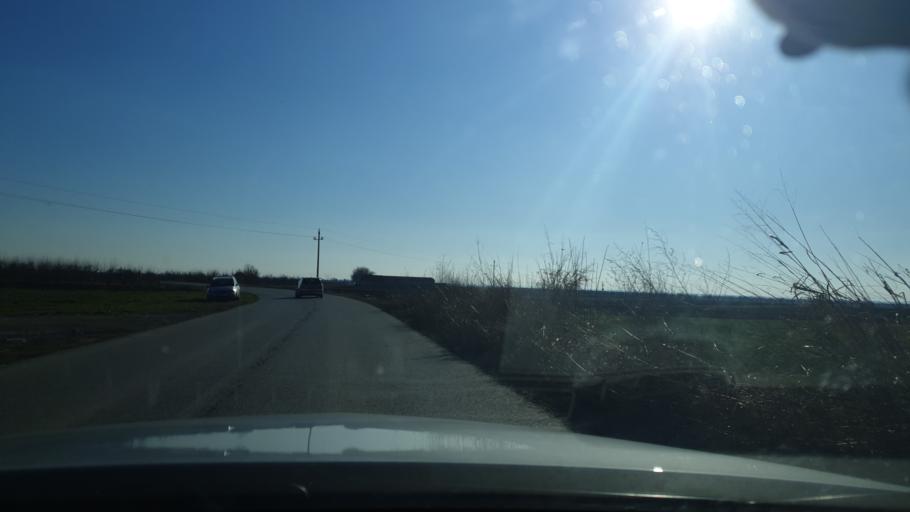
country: RS
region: Autonomna Pokrajina Vojvodina
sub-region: Sremski Okrug
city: Ruma
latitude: 45.0440
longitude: 19.8045
